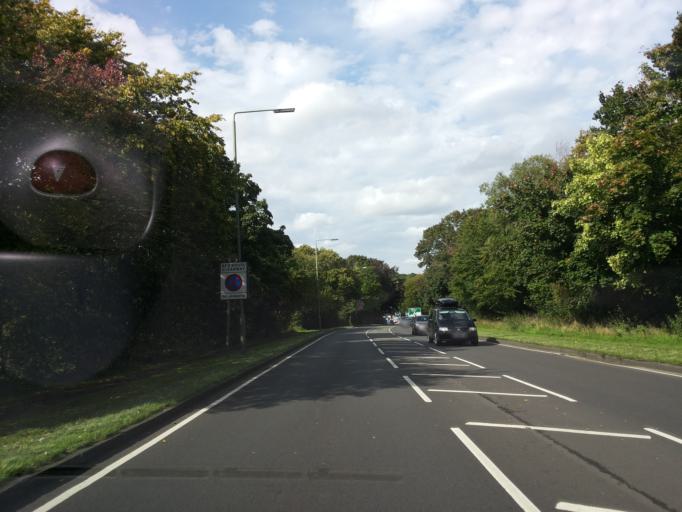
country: GB
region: England
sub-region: Greater London
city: Orpington
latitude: 51.3473
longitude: 0.0909
